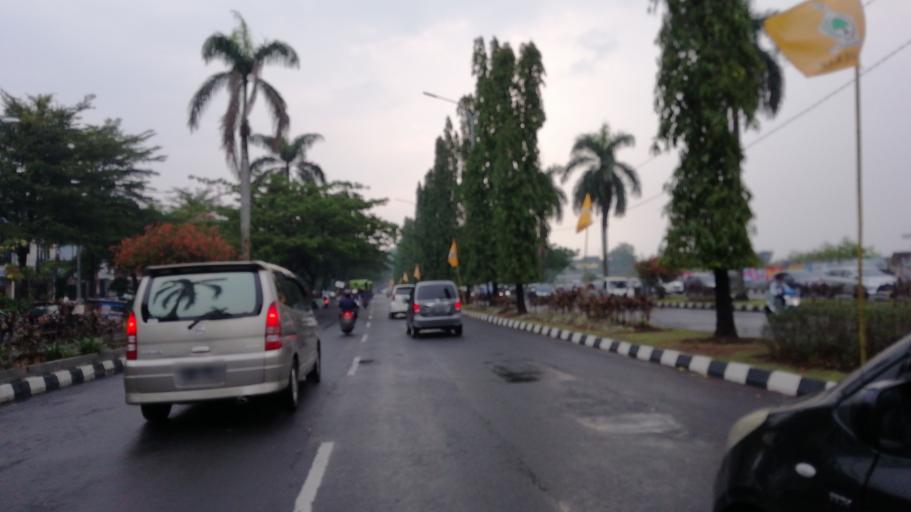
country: ID
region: West Java
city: Cibinong
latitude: -6.4850
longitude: 106.8413
